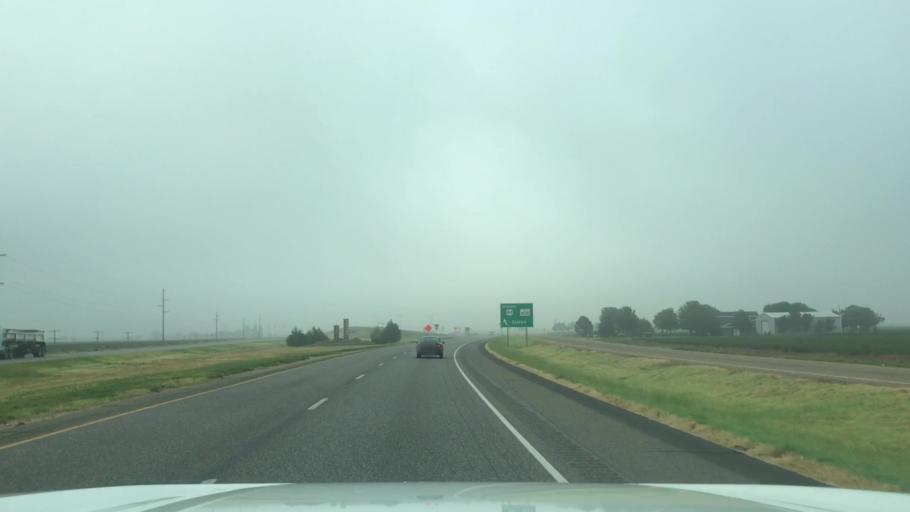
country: US
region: Texas
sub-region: Lubbock County
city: Slaton
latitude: 33.4612
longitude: -101.6725
